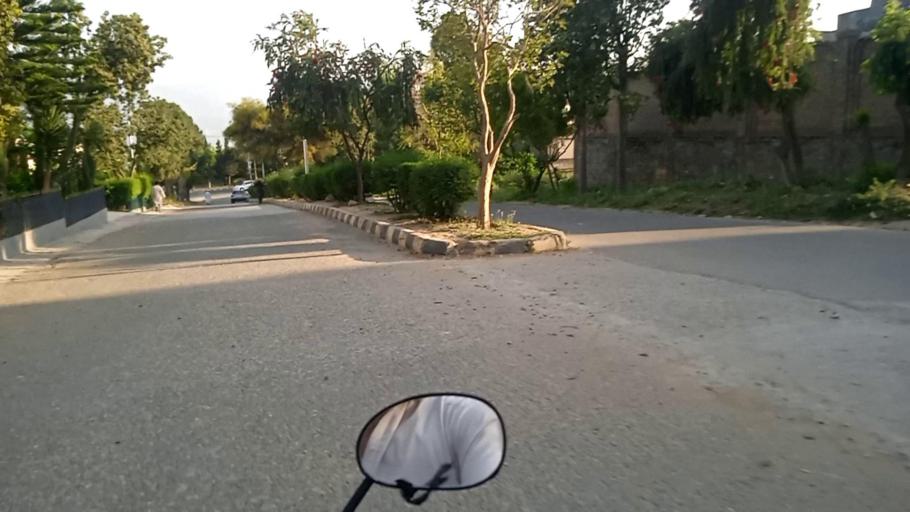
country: PK
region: Khyber Pakhtunkhwa
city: Mingora
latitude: 34.8309
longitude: 72.3425
